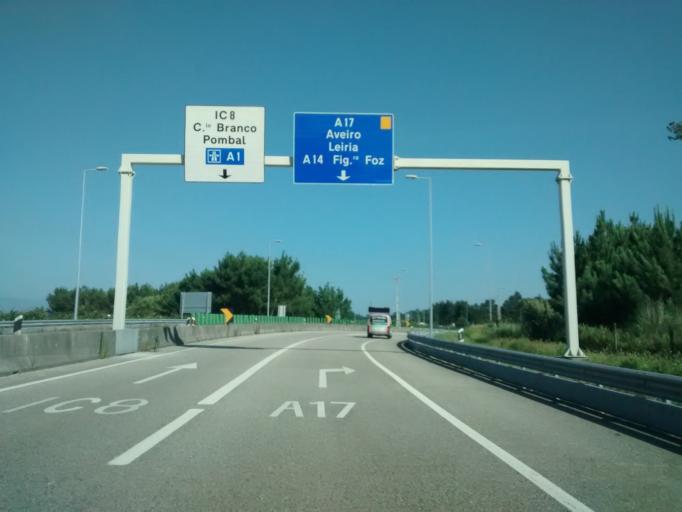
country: PT
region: Leiria
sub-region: Pombal
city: Lourical
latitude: 39.9906
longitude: -8.7892
